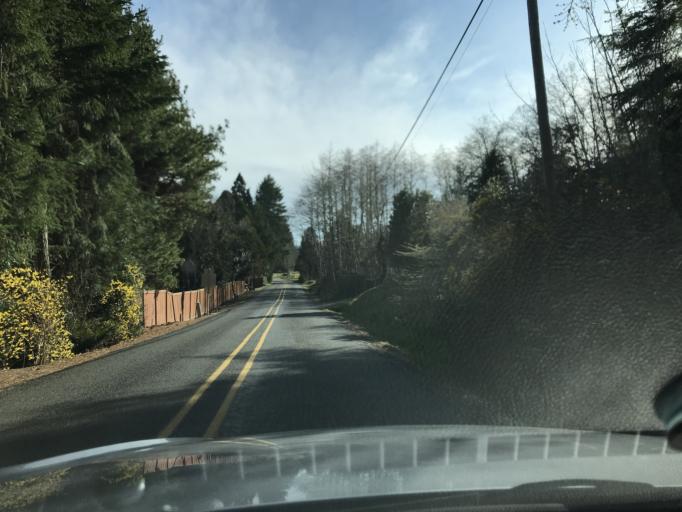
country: US
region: Washington
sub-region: Pierce County
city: Home
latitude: 47.2553
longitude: -122.7590
